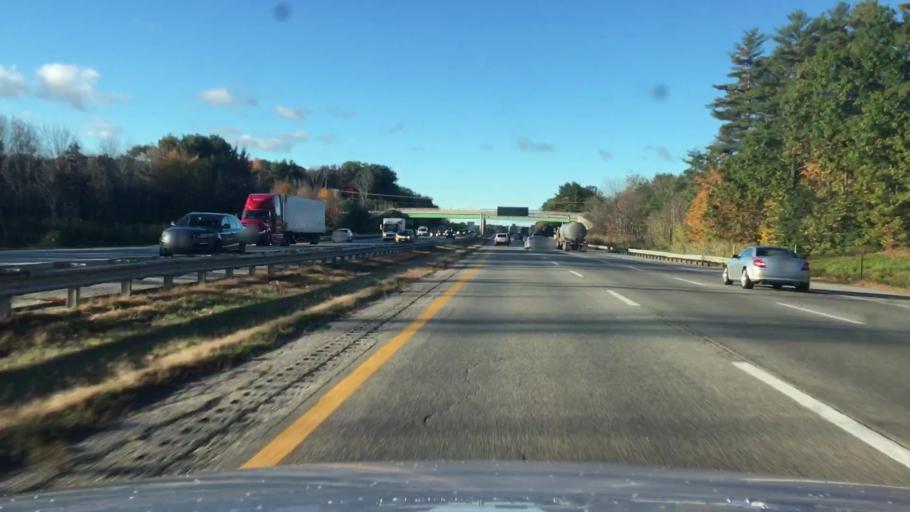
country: US
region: Maine
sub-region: Cumberland County
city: West Scarborough
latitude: 43.6015
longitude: -70.3763
